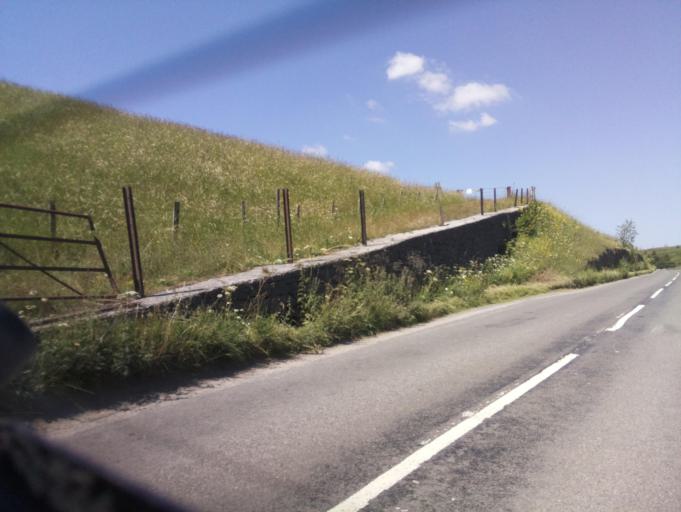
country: GB
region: England
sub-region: Derbyshire
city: Buxton
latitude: 53.2901
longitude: -1.8658
